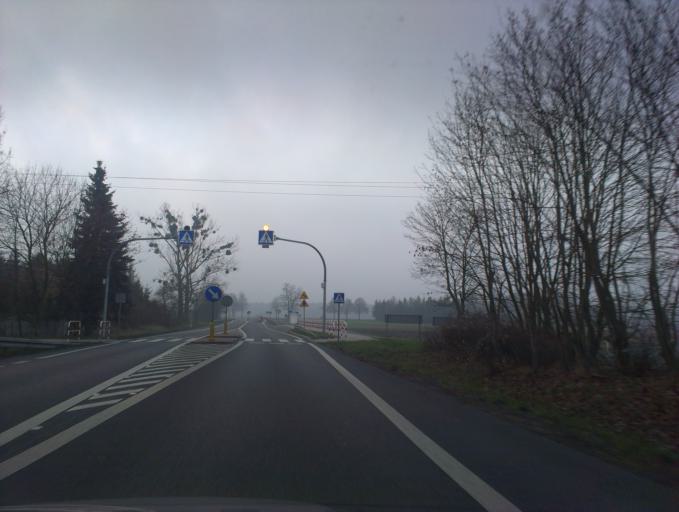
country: PL
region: Greater Poland Voivodeship
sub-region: Powiat chodzieski
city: Chodziez
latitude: 52.9543
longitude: 16.9398
